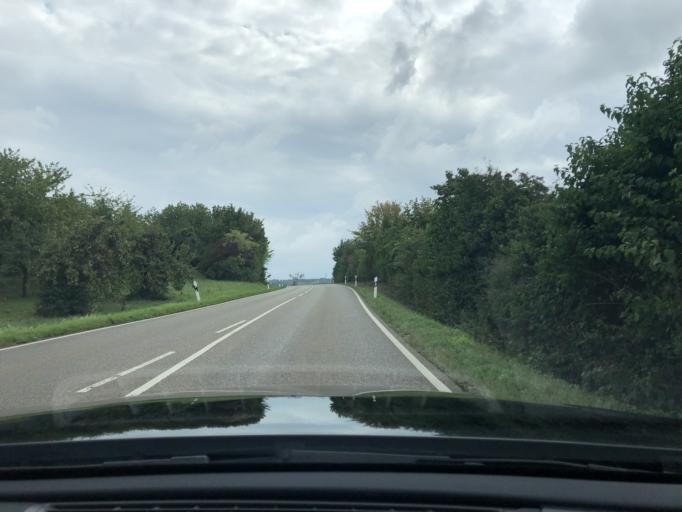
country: DE
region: Baden-Wuerttemberg
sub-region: Regierungsbezirk Stuttgart
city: Marbach am Neckar
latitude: 48.9321
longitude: 9.2777
